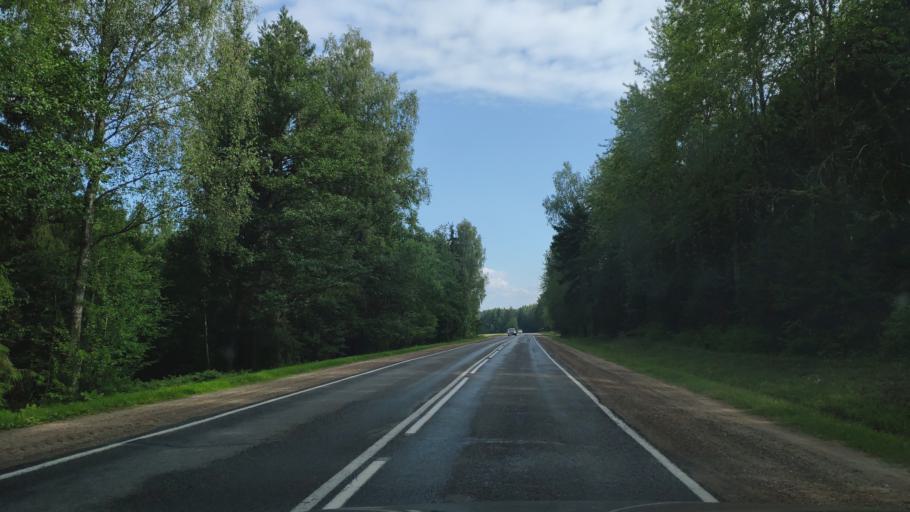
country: BY
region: Minsk
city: Zaslawye
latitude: 53.9662
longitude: 27.2450
